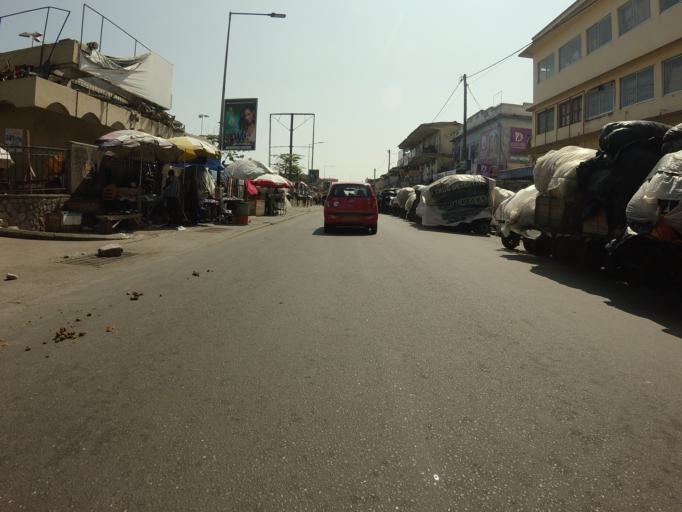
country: GH
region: Greater Accra
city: Accra
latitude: 5.5462
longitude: -0.2071
